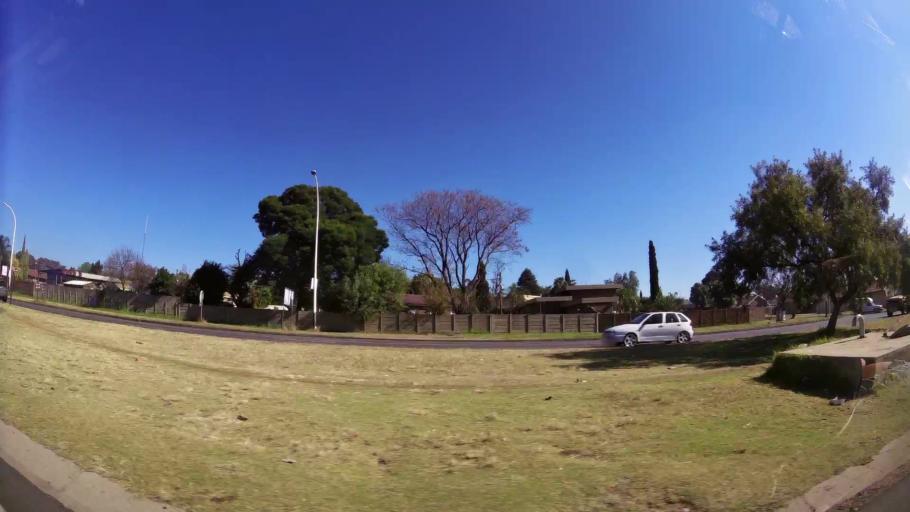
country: ZA
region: Mpumalanga
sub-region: Nkangala District Municipality
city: Witbank
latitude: -25.8718
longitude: 29.2397
